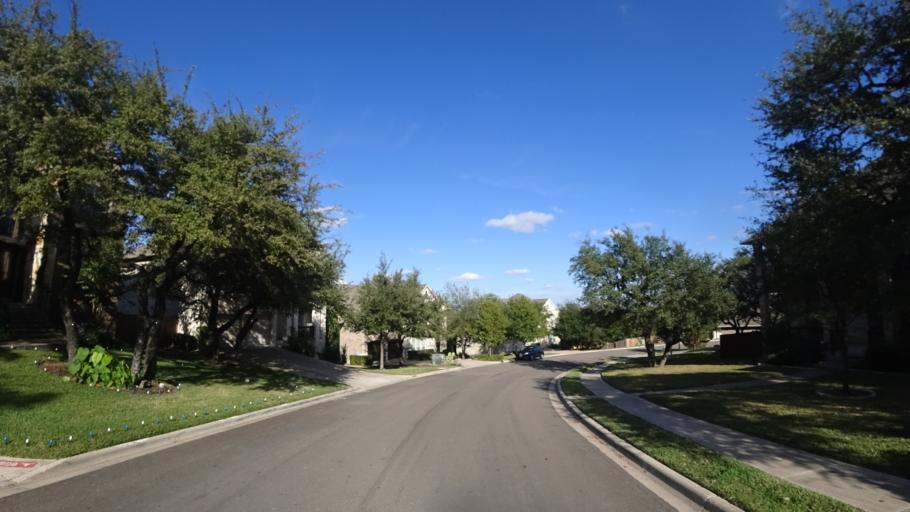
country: US
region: Texas
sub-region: Travis County
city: Barton Creek
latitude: 30.2473
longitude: -97.8754
